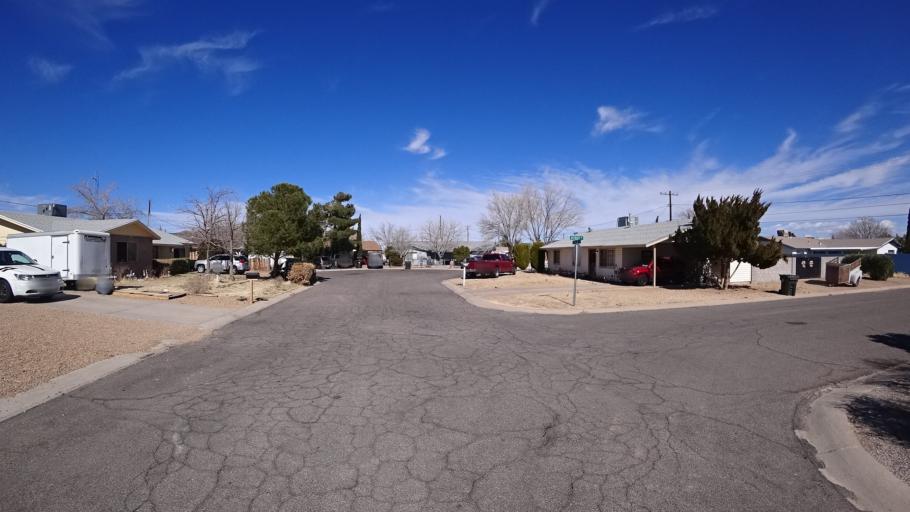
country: US
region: Arizona
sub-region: Mohave County
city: Kingman
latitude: 35.2139
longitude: -114.0427
